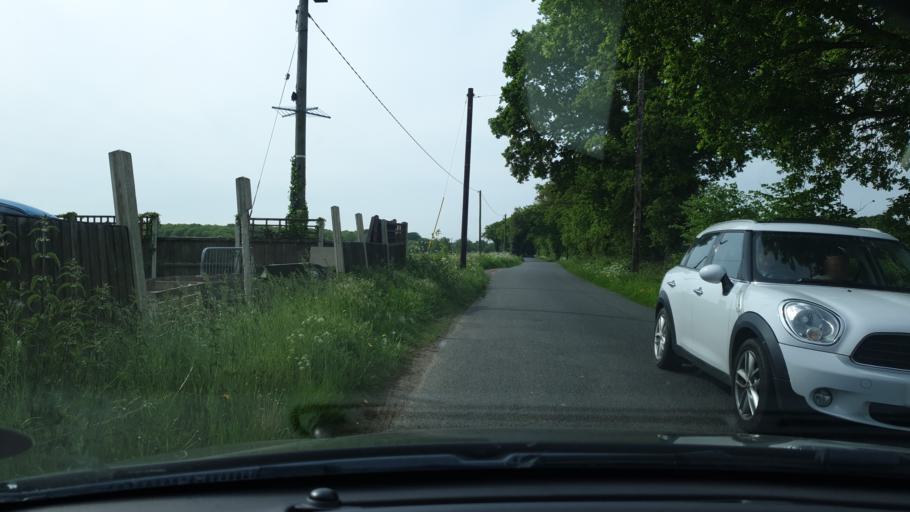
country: GB
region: England
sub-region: Essex
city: Little Clacton
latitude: 51.8401
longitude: 1.1045
